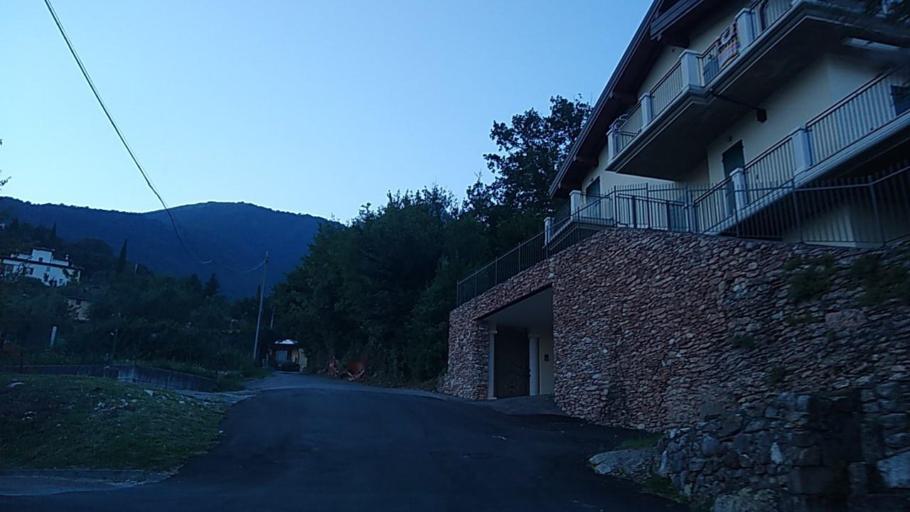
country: IT
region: Lombardy
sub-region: Provincia di Brescia
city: Toscolano Maderno
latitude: 45.6431
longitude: 10.6054
